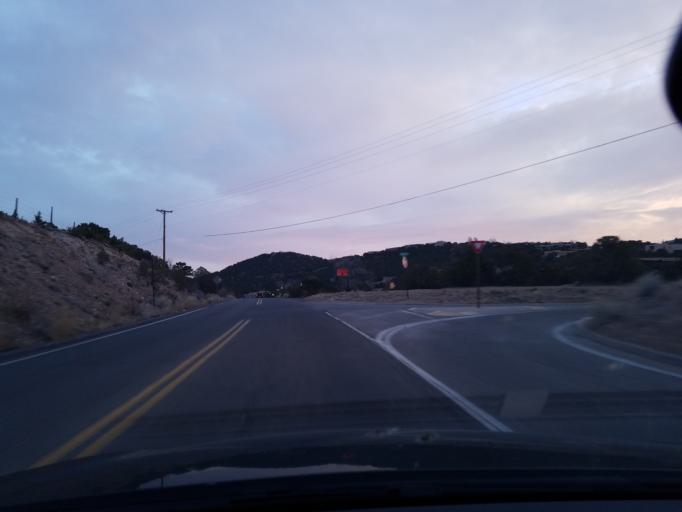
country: US
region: New Mexico
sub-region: Santa Fe County
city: Santa Fe
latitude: 35.6959
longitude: -105.9120
